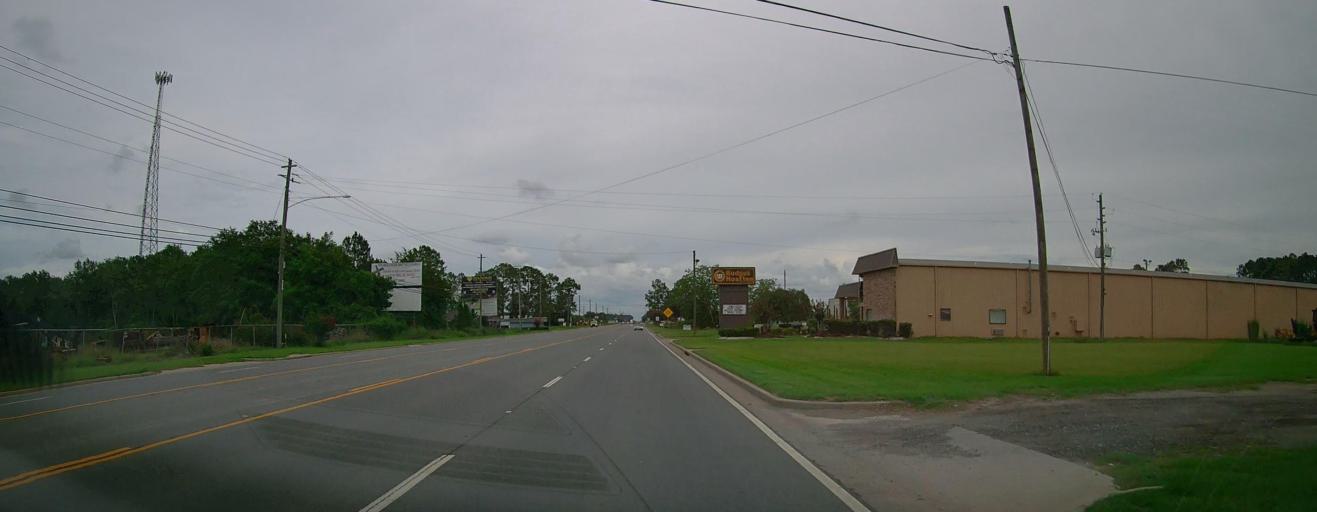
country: US
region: Georgia
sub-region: Appling County
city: Baxley
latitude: 31.7738
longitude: -82.3348
